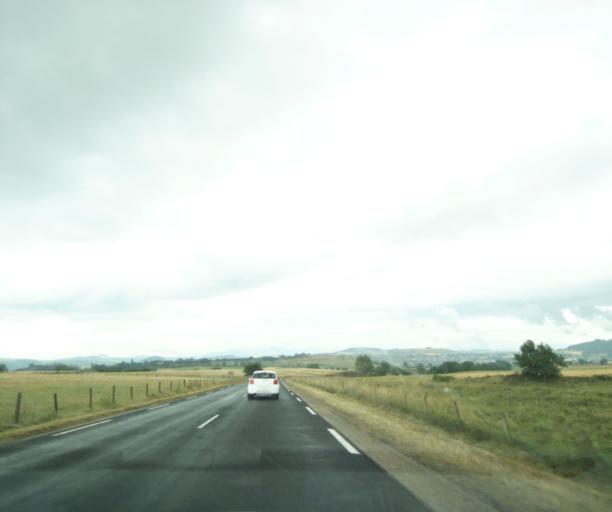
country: FR
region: Auvergne
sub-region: Departement de la Haute-Loire
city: Espaly-Saint-Marcel
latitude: 45.0341
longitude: 3.8563
